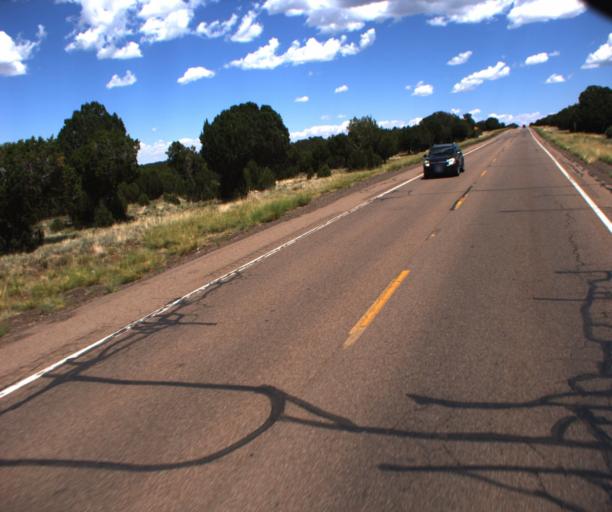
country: US
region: Arizona
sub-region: Navajo County
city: White Mountain Lake
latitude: 34.2726
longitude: -109.9134
